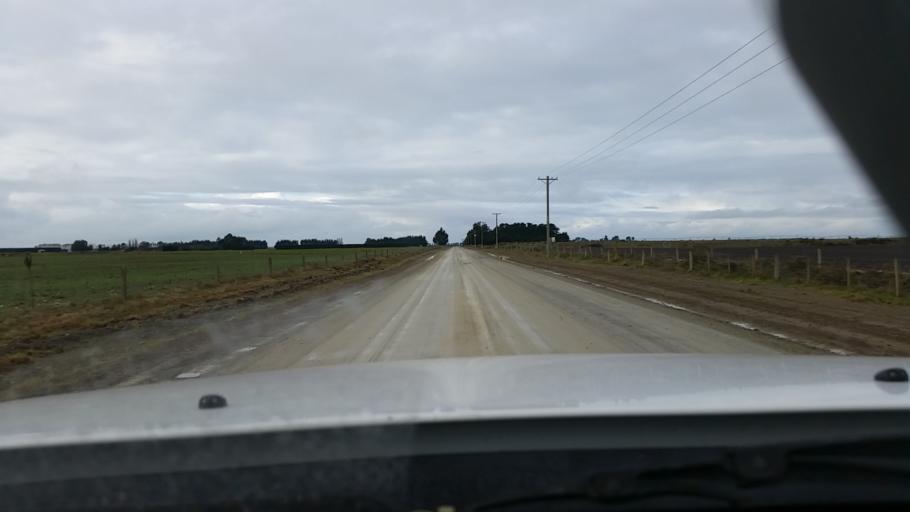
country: NZ
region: Canterbury
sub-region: Timaru District
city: Timaru
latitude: -44.1405
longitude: 171.4150
